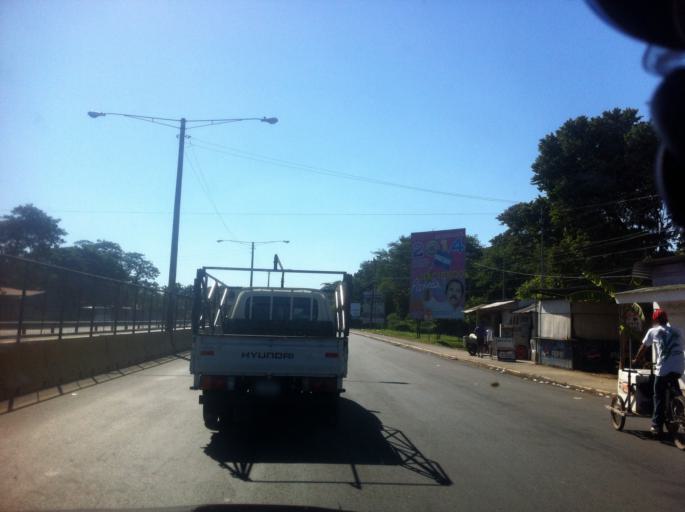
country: NI
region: Managua
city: Tipitapa
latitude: 12.1490
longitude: -86.1577
